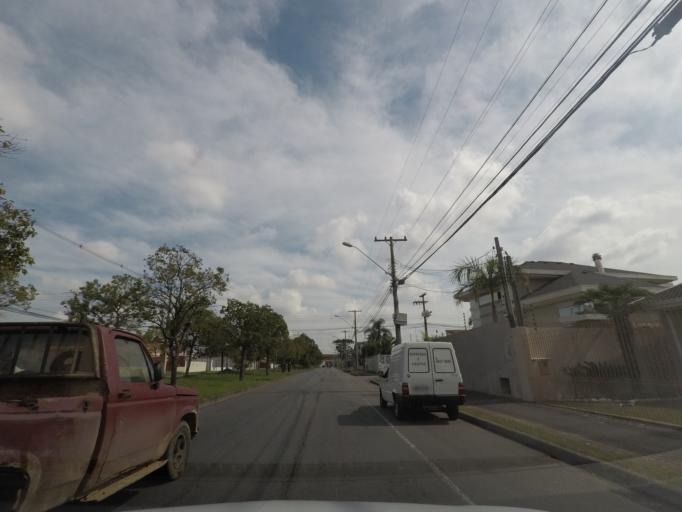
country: BR
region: Parana
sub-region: Pinhais
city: Pinhais
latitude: -25.4719
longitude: -49.2077
